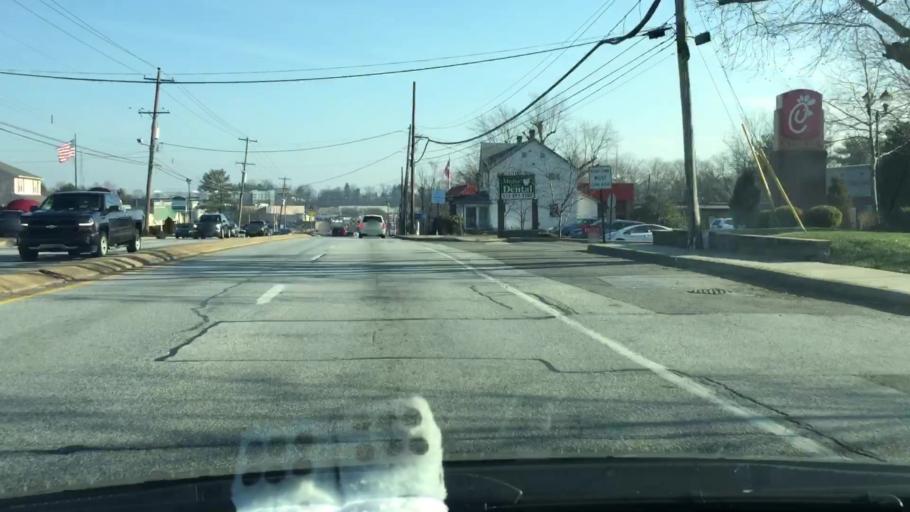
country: US
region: Pennsylvania
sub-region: Delaware County
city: Lima
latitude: 39.9124
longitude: -75.4392
